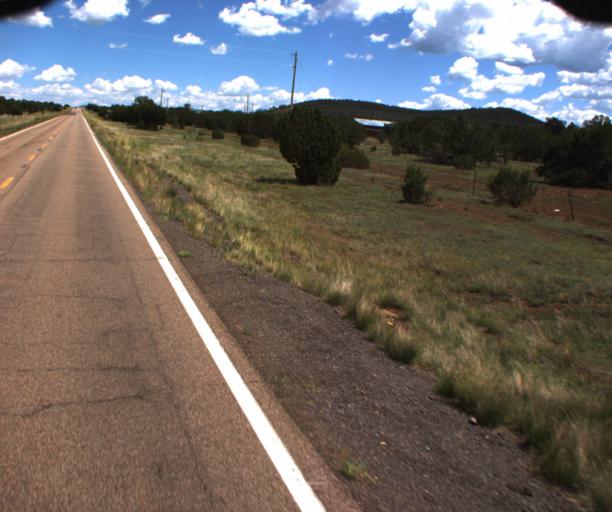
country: US
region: Arizona
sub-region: Navajo County
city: Pinetop-Lakeside
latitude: 34.2744
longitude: -109.7710
